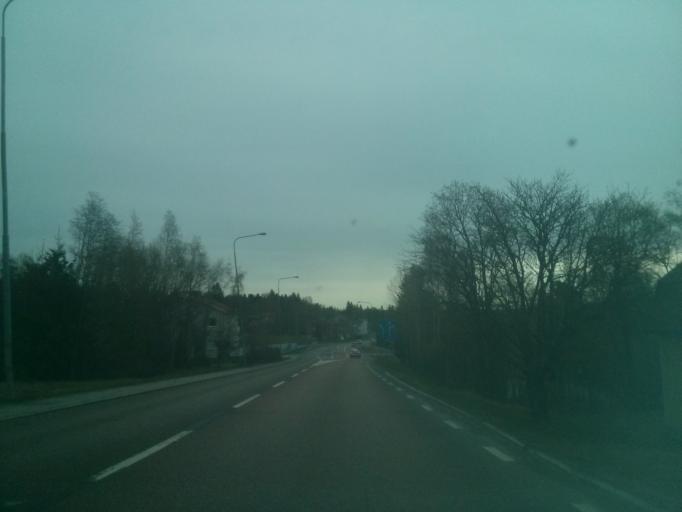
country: SE
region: Vaesternorrland
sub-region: Haernoesands Kommun
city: Haernoesand
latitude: 62.6178
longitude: 17.9093
